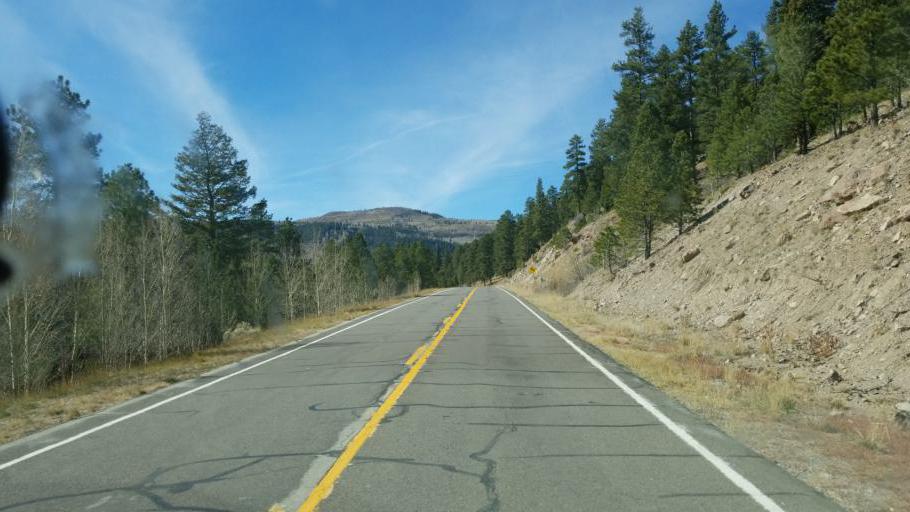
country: US
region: Colorado
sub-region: Conejos County
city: Conejos
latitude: 37.0748
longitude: -106.2815
